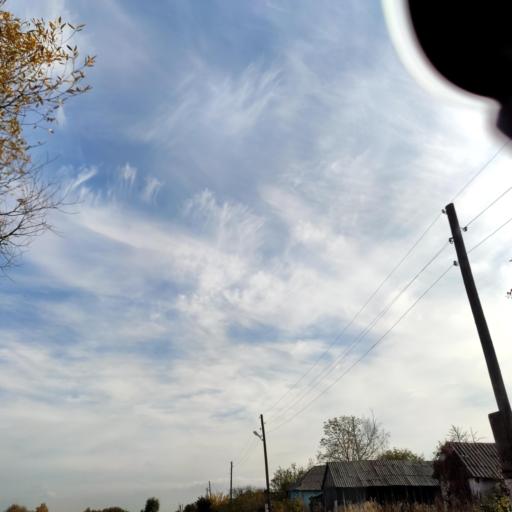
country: RU
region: Voronezj
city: Rossosh'
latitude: 51.1967
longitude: 38.7736
